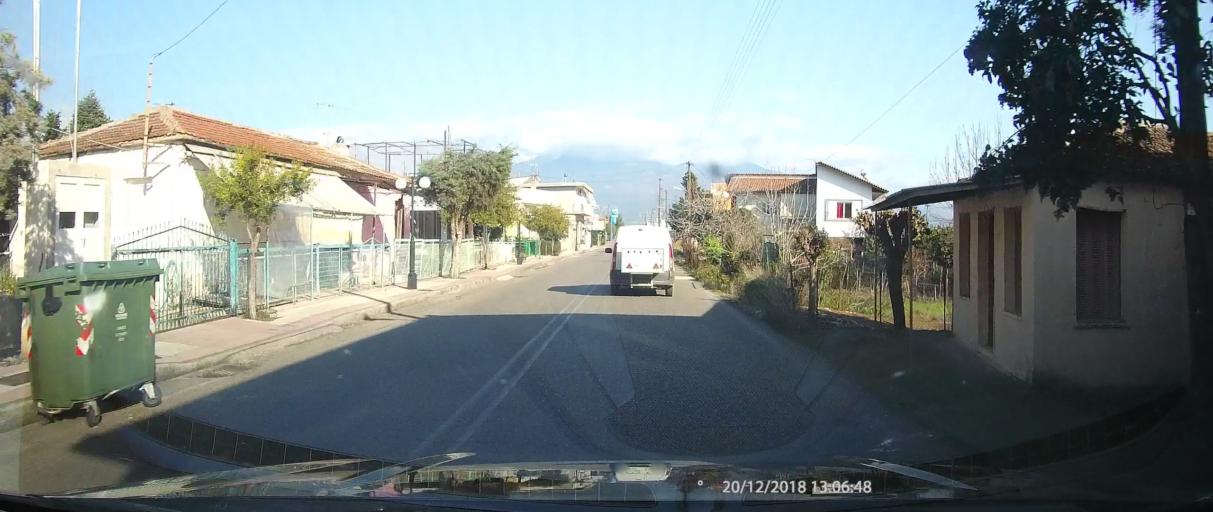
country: GR
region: West Greece
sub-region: Nomos Aitolias kai Akarnanias
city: Panaitolion
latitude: 38.5849
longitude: 21.4510
